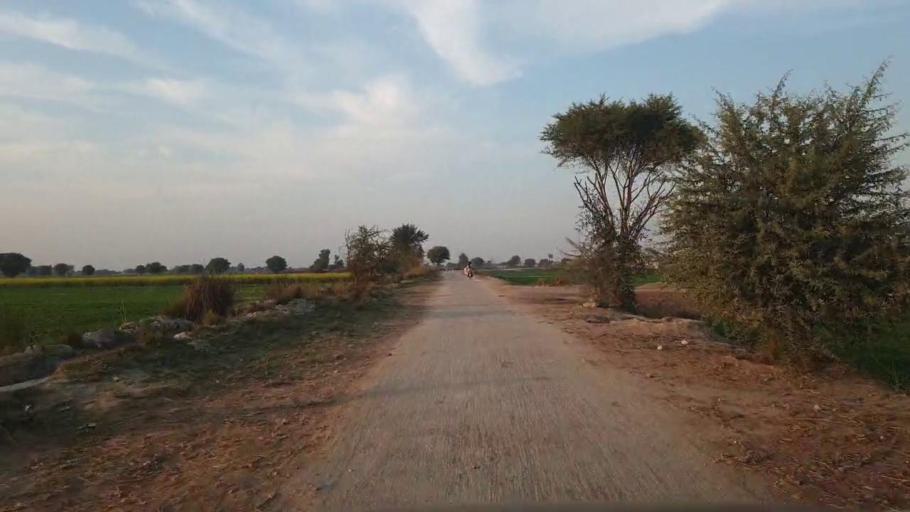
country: PK
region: Sindh
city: Shahpur Chakar
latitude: 26.1882
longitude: 68.6170
